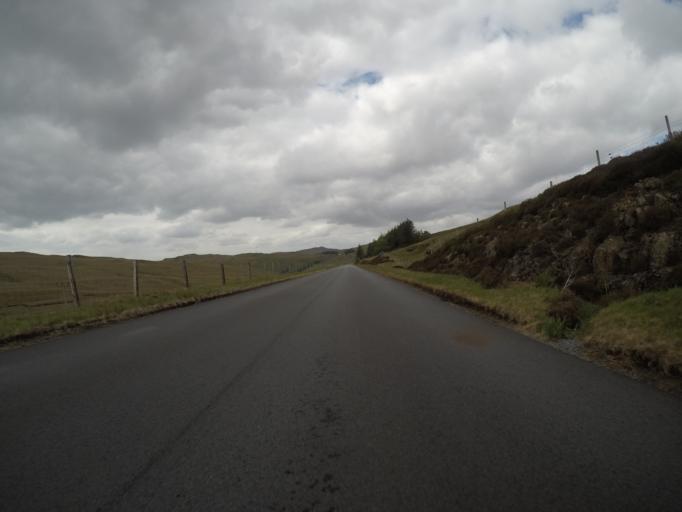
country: GB
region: Scotland
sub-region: Highland
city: Isle of Skye
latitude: 57.3224
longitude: -6.3289
